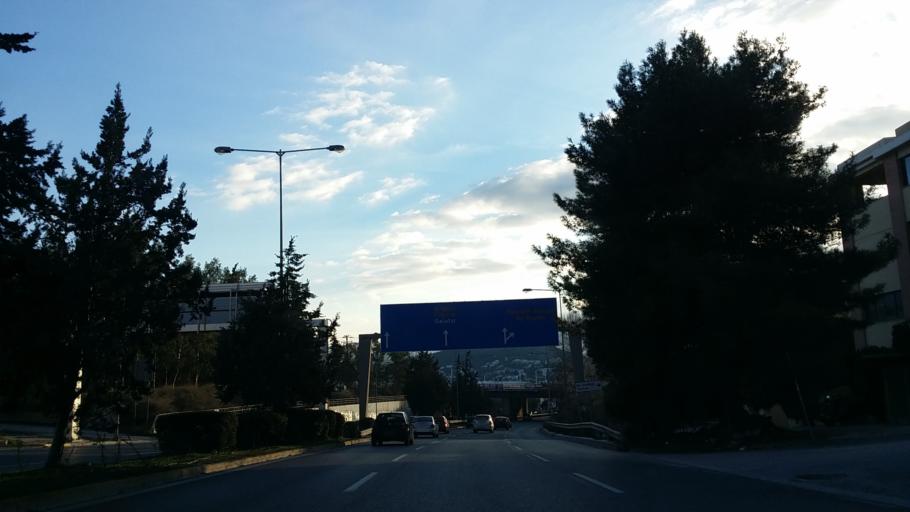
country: GR
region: Attica
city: Pefki
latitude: 38.0464
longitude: 23.7824
